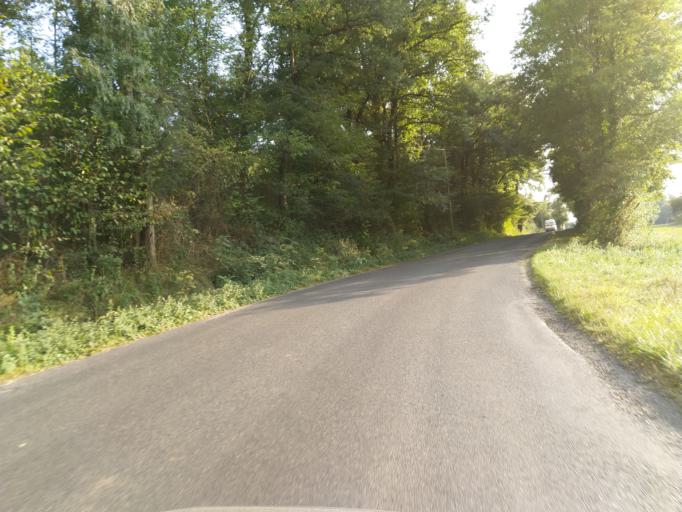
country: FR
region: Midi-Pyrenees
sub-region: Departement du Tarn
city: Frejairolles
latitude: 43.8534
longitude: 2.2386
